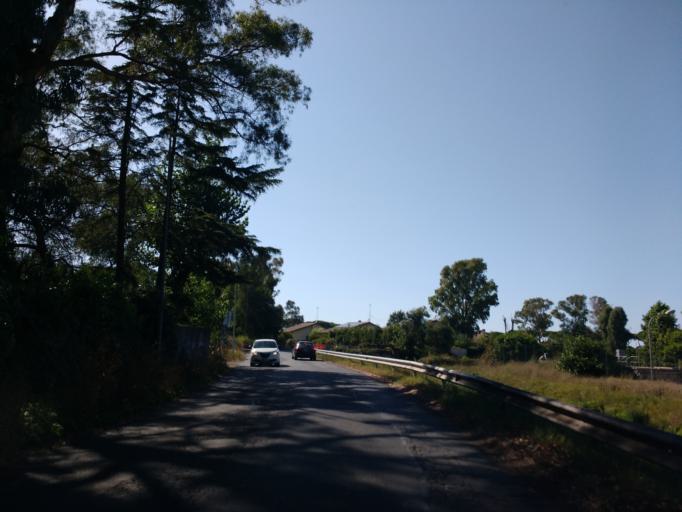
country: IT
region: Latium
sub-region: Citta metropolitana di Roma Capitale
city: Acilia-Castel Fusano-Ostia Antica
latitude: 41.7493
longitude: 12.3312
